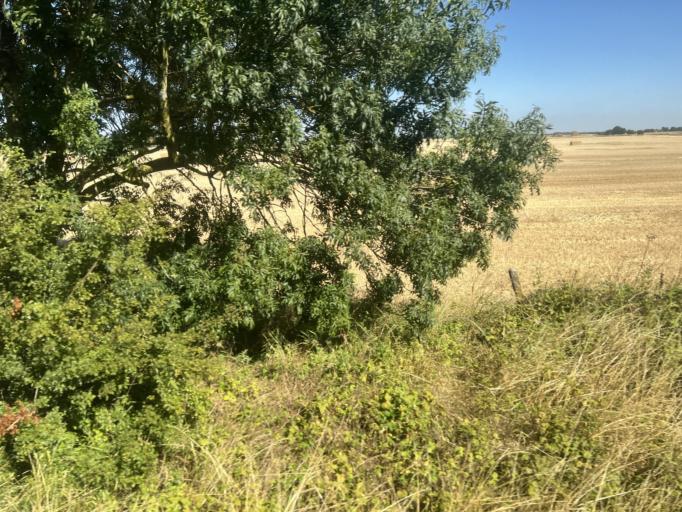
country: GB
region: England
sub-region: Lincolnshire
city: Donington
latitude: 52.9665
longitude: -0.2269
